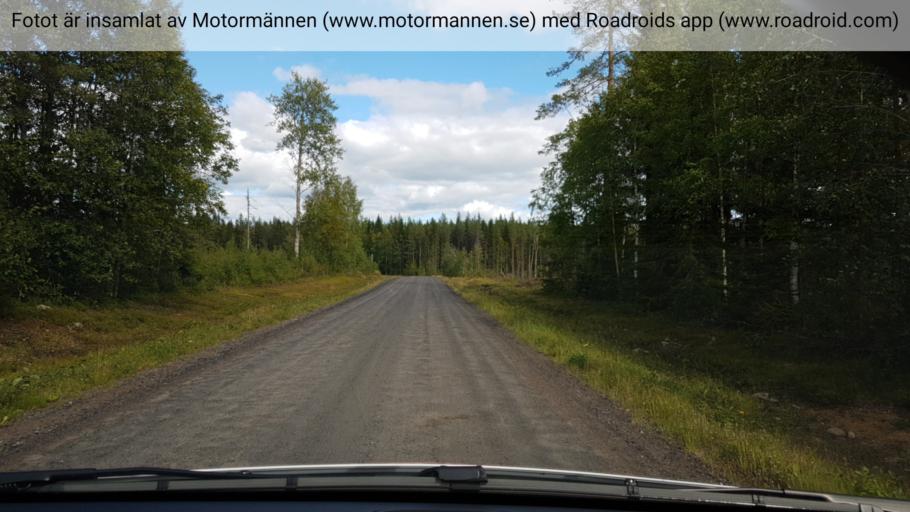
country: SE
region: Vaesterbotten
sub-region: Nordmalings Kommun
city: Nordmaling
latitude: 63.6765
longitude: 19.6752
